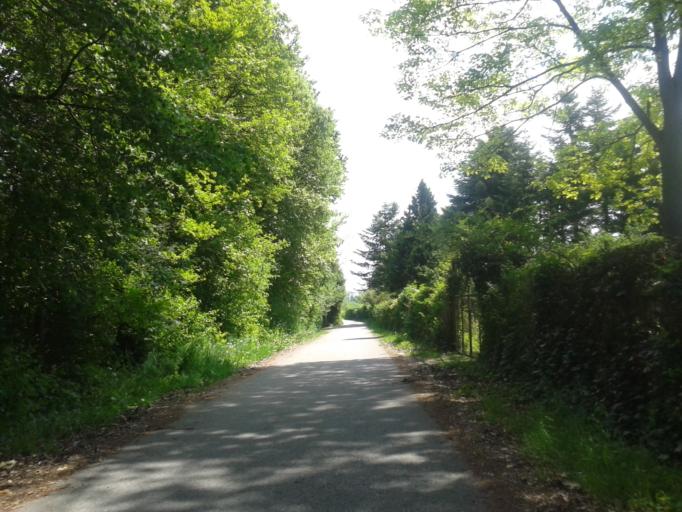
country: DE
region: Baden-Wuerttemberg
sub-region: Tuebingen Region
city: Erbach
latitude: 48.3246
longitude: 9.9108
